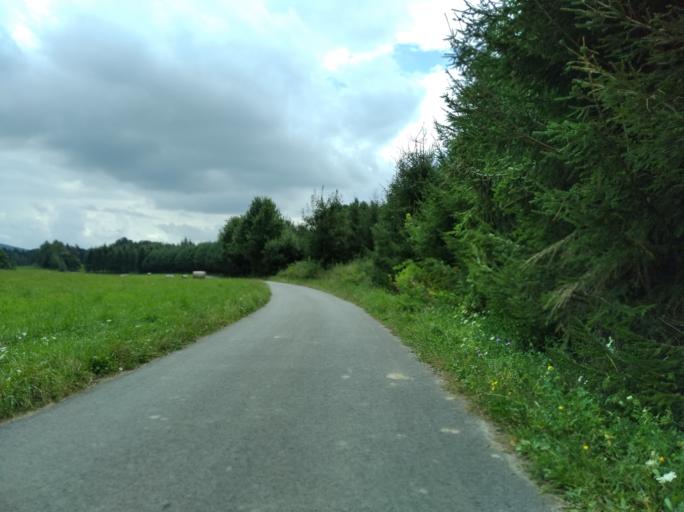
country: PL
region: Subcarpathian Voivodeship
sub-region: Powiat krosnienski
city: Odrzykon
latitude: 49.7787
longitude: 21.7240
